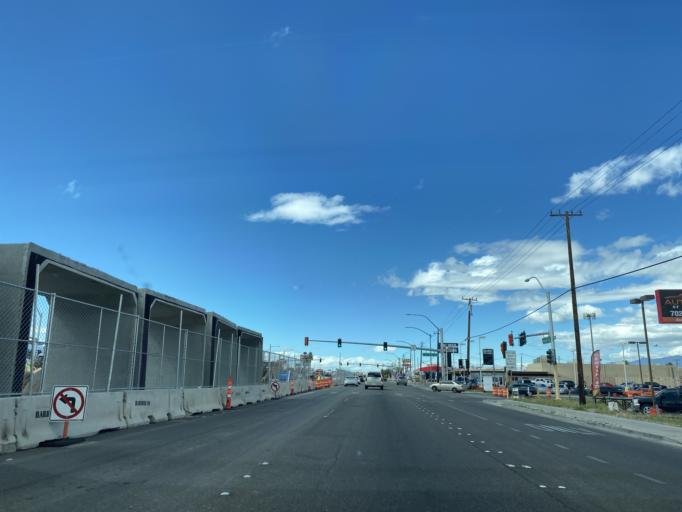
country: US
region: Nevada
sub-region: Clark County
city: Winchester
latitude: 36.1482
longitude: -115.1041
